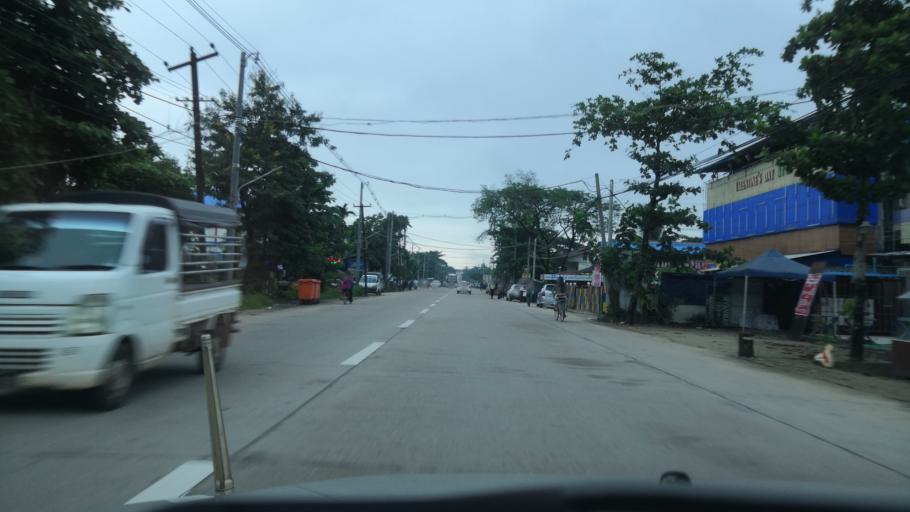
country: MM
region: Yangon
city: Yangon
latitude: 16.8800
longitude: 96.1705
